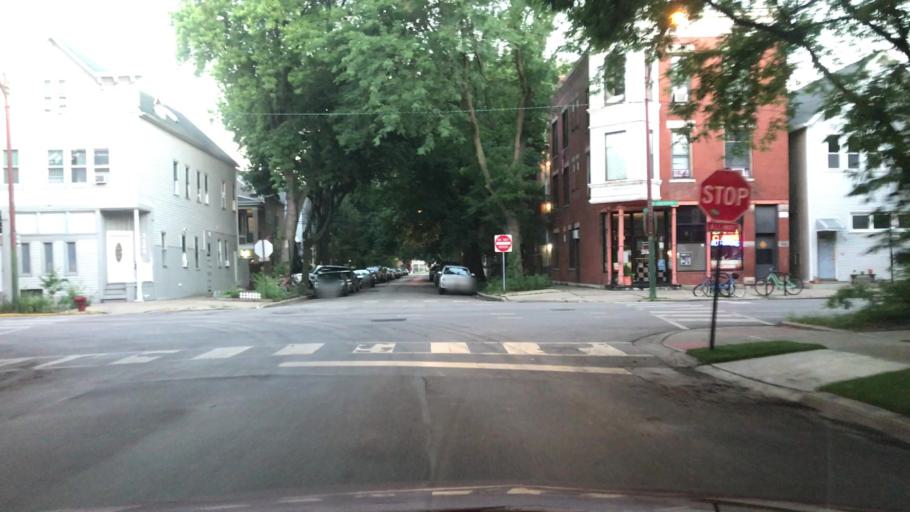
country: US
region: Illinois
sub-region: Cook County
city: Chicago
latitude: 41.9389
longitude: -87.6635
